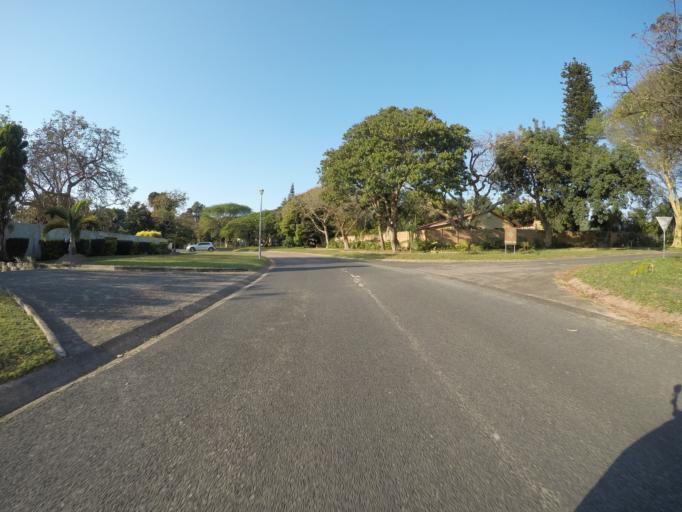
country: ZA
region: KwaZulu-Natal
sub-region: uThungulu District Municipality
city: Richards Bay
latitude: -28.7741
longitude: 32.1060
